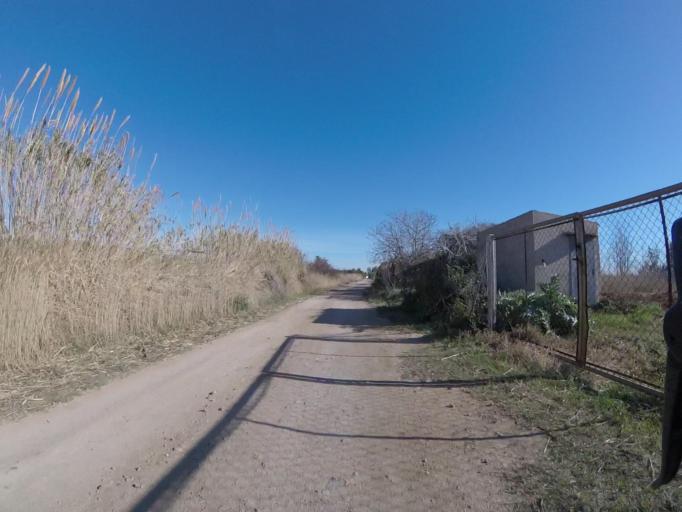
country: ES
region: Valencia
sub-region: Provincia de Castello
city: Orpesa/Oropesa del Mar
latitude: 40.1445
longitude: 0.1645
